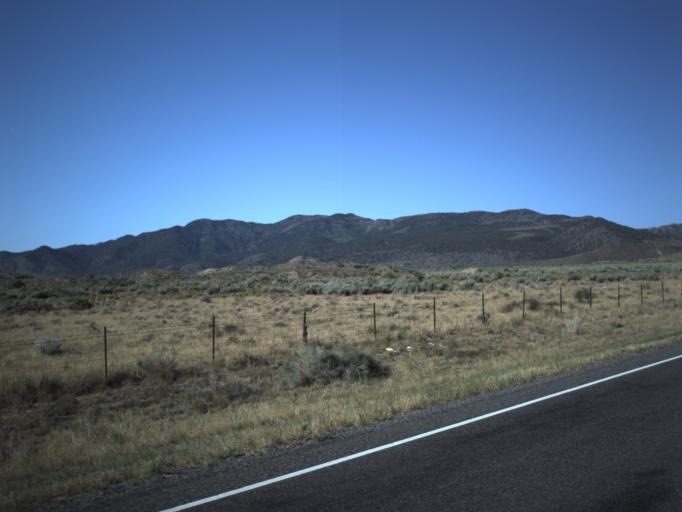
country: US
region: Utah
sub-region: Utah County
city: Genola
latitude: 39.9517
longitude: -111.9823
